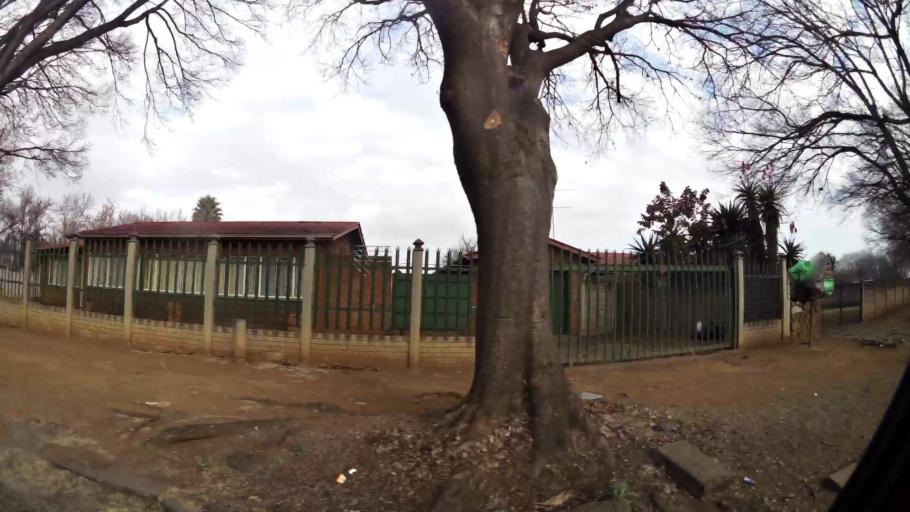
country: ZA
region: Gauteng
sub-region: Sedibeng District Municipality
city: Vanderbijlpark
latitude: -26.6840
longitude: 27.8144
